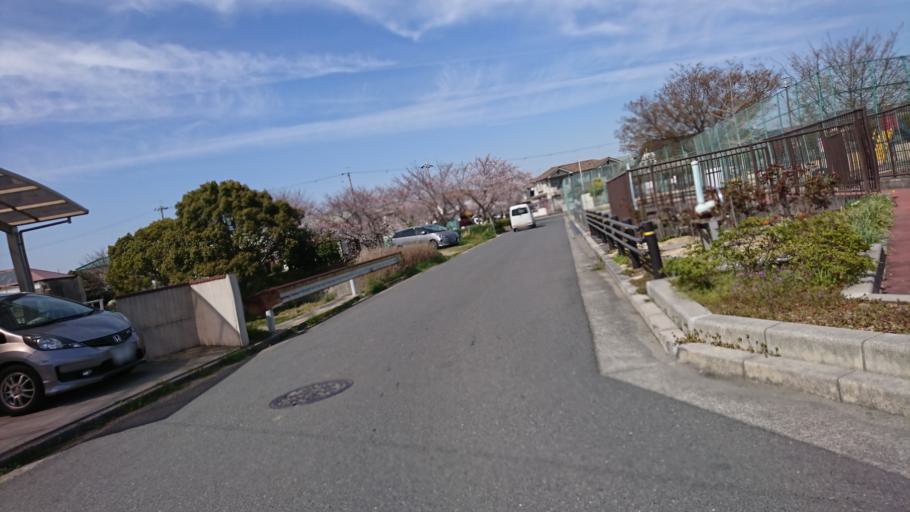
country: JP
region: Hyogo
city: Kakogawacho-honmachi
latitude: 34.7503
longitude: 134.9030
